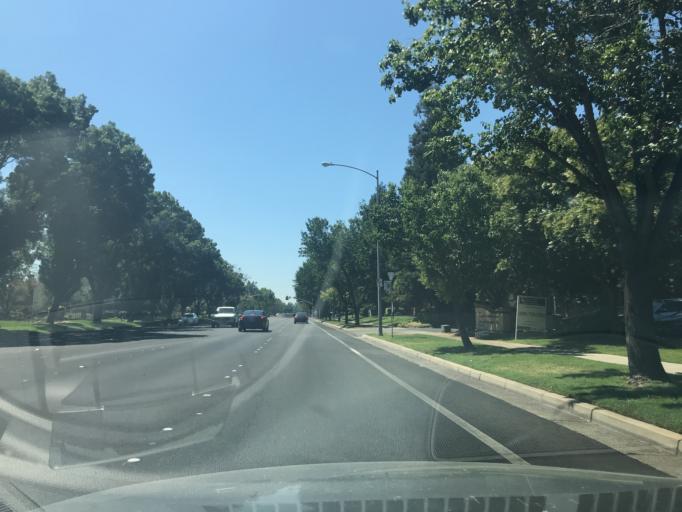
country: US
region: California
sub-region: Merced County
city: Merced
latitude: 37.3245
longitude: -120.4784
